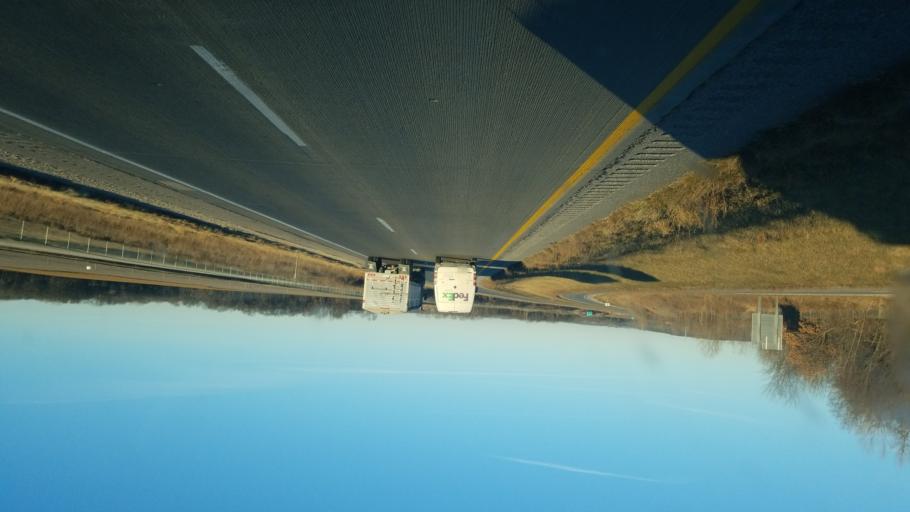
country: US
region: Iowa
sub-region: Wapello County
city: Eddyville
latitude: 41.1648
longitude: -92.6238
